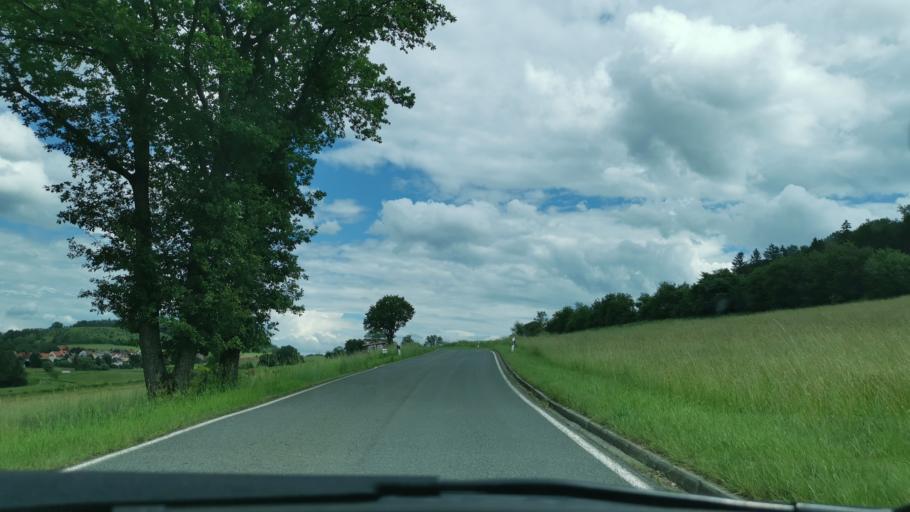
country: DE
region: Hesse
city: Hessisch Lichtenau
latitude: 51.1607
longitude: 9.7601
